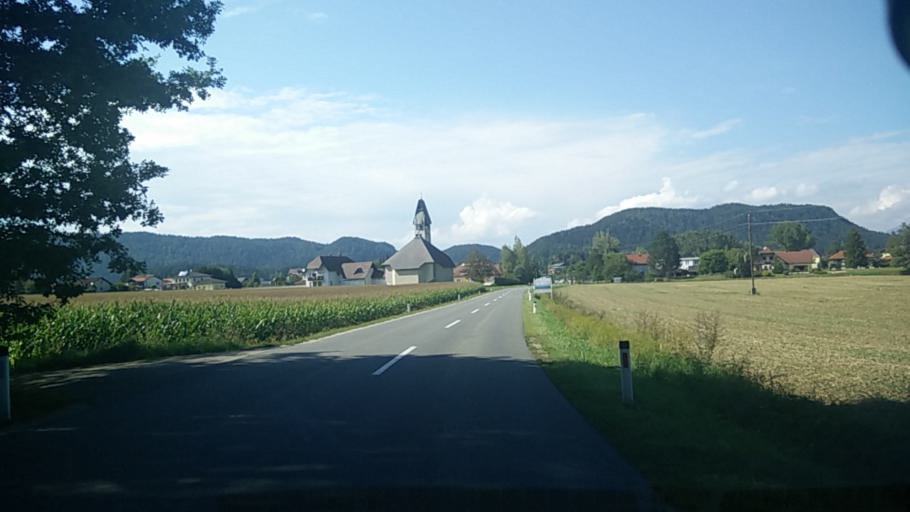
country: AT
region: Carinthia
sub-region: Politischer Bezirk Volkermarkt
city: Sittersdorf
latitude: 46.5739
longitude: 14.5660
